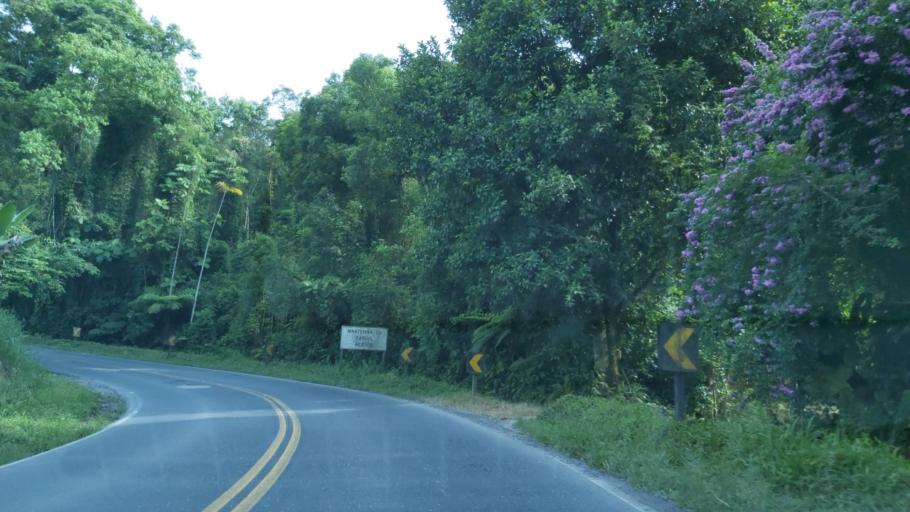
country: BR
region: Sao Paulo
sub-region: Juquia
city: Juquia
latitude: -24.1117
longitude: -47.6248
